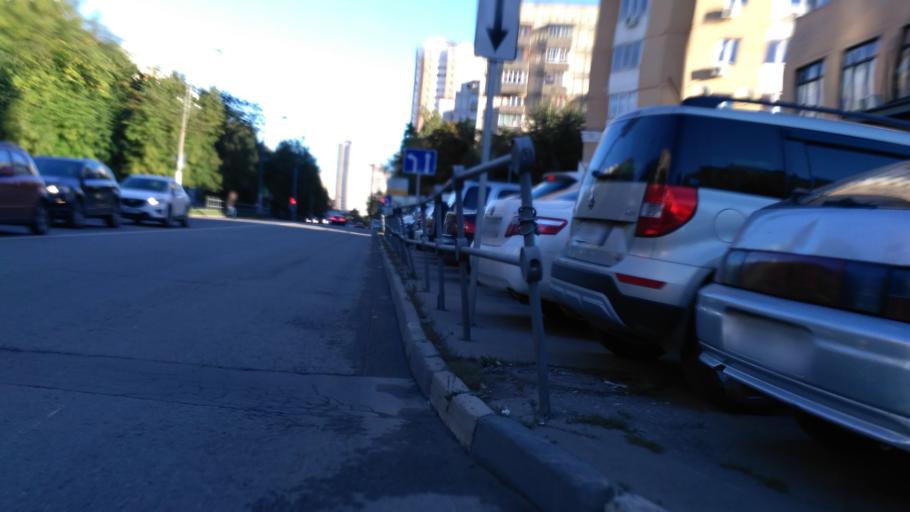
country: RU
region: Moskovskaya
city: Vostochnoe Degunino
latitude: 55.8678
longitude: 37.5578
